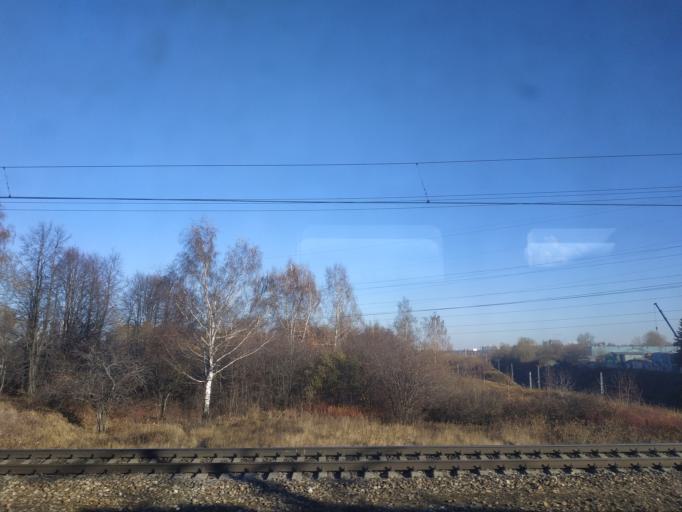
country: RU
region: Moscow
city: Tsaritsyno
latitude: 55.6102
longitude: 37.6415
